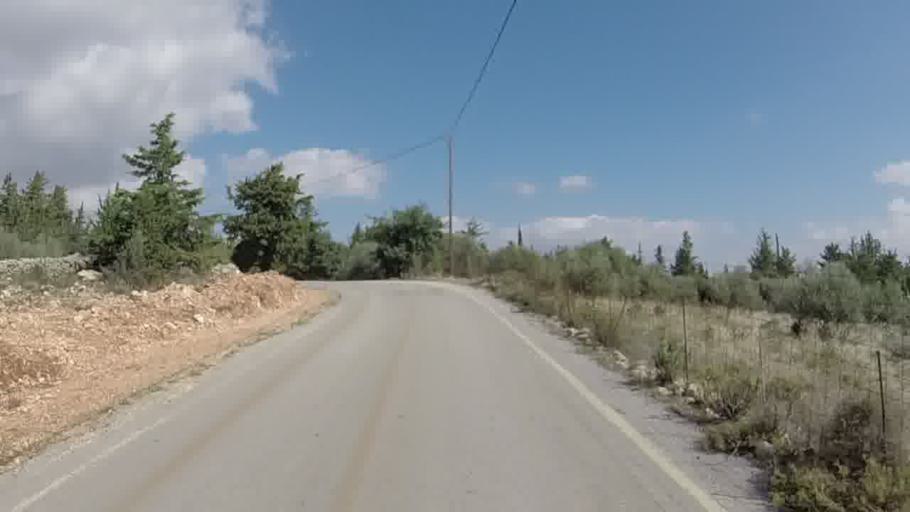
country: GR
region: Crete
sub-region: Nomos Chanias
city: Kalivai
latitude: 35.3904
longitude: 24.1276
